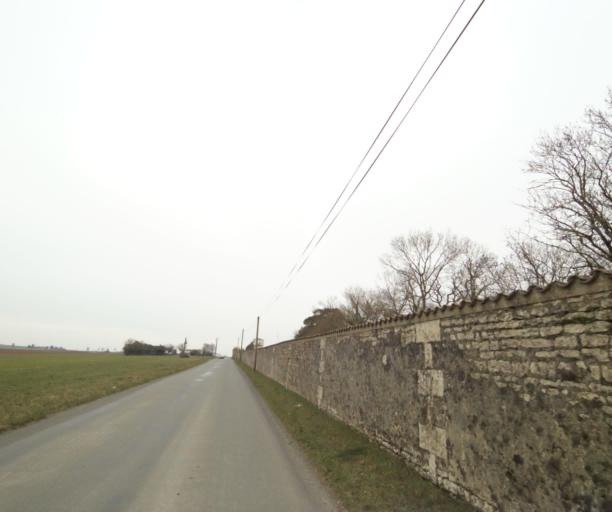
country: FR
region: Poitou-Charentes
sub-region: Departement des Deux-Sevres
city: Bessines
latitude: 46.3344
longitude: -0.5166
